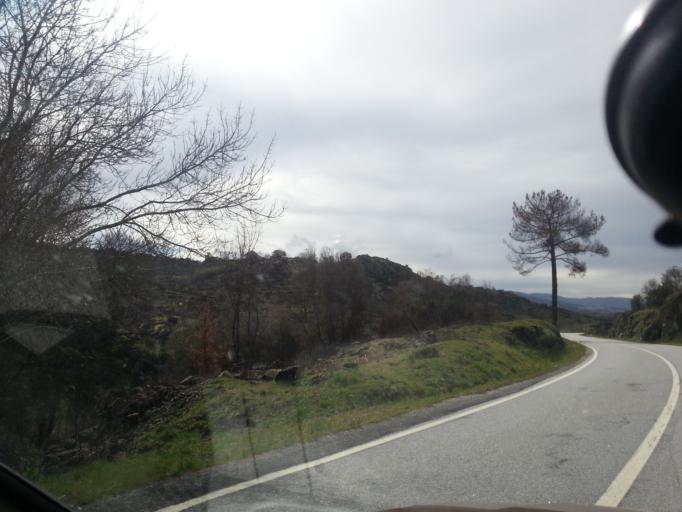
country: PT
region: Guarda
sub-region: Fornos de Algodres
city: Fornos de Algodres
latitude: 40.5674
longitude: -7.5560
